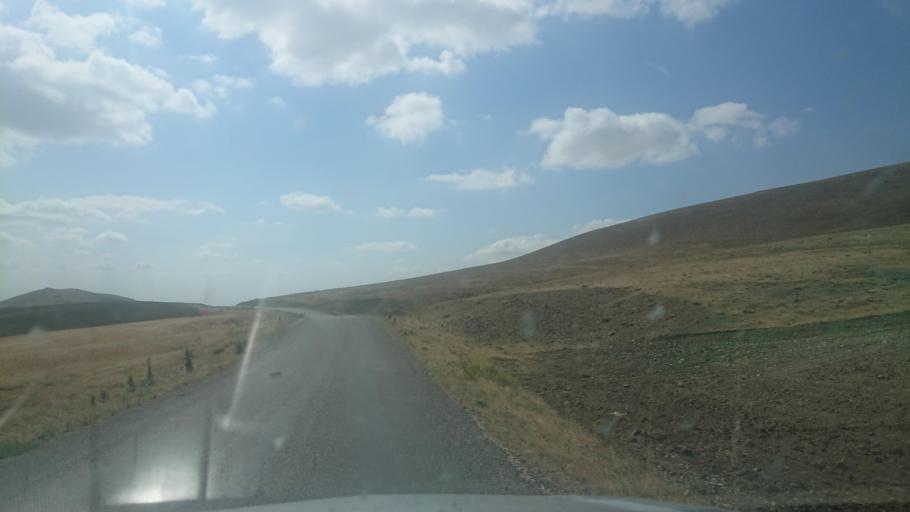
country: TR
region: Aksaray
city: Sariyahsi
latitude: 39.0027
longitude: 33.9698
